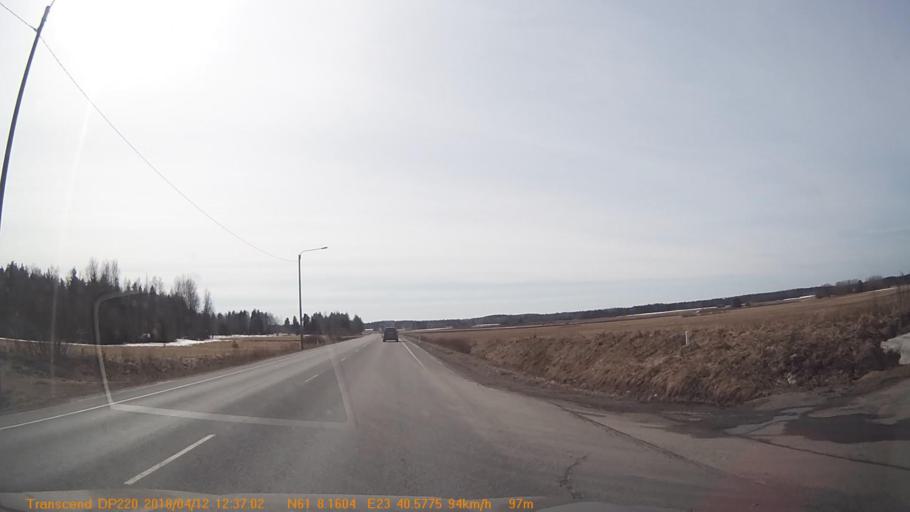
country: FI
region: Pirkanmaa
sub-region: Etelae-Pirkanmaa
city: Kylmaekoski
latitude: 61.1361
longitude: 23.6764
